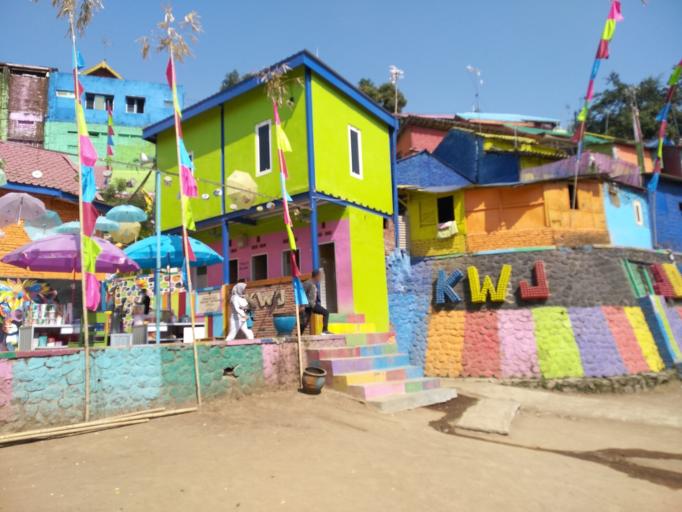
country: ID
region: East Java
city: Malang
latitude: -7.9830
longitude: 112.6378
